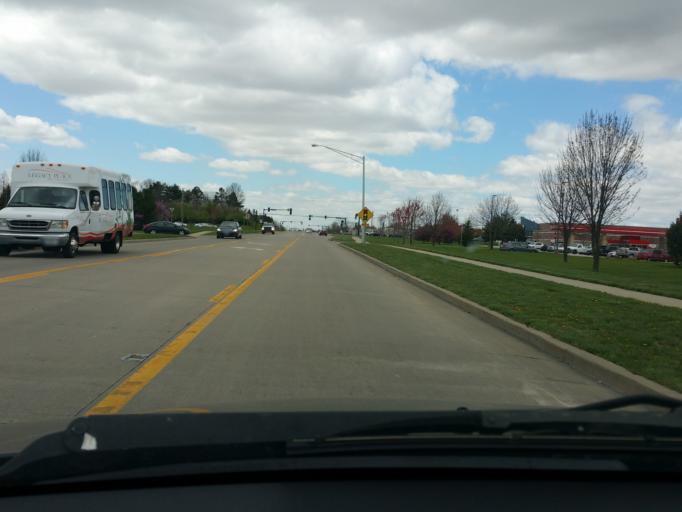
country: US
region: Illinois
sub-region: Madison County
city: Edwardsville
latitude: 38.7873
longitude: -89.9483
